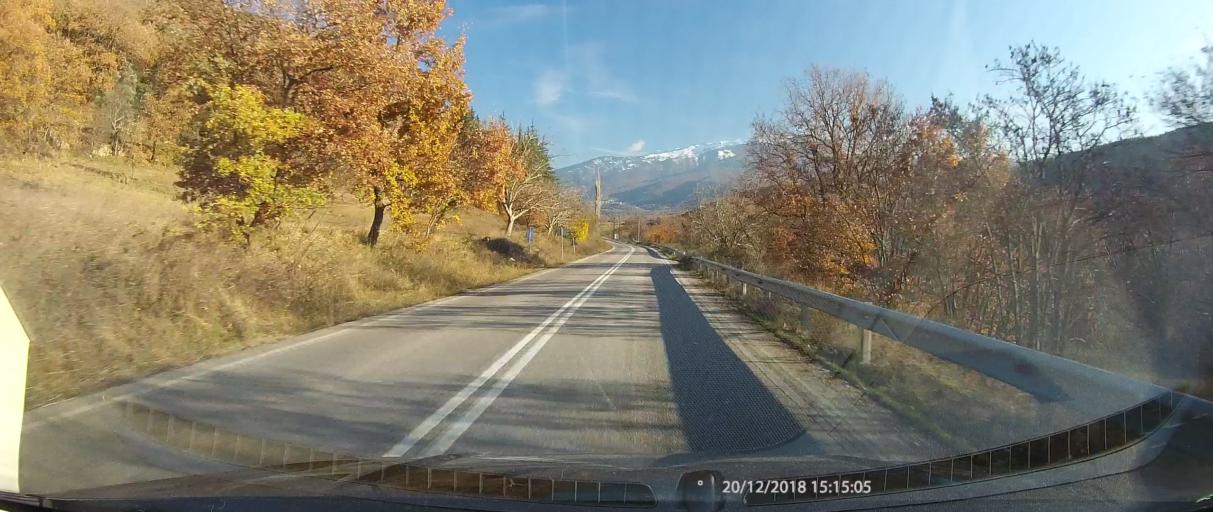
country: GR
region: Central Greece
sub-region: Nomos Fthiotidos
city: Makrakomi
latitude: 38.9309
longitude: 21.9868
